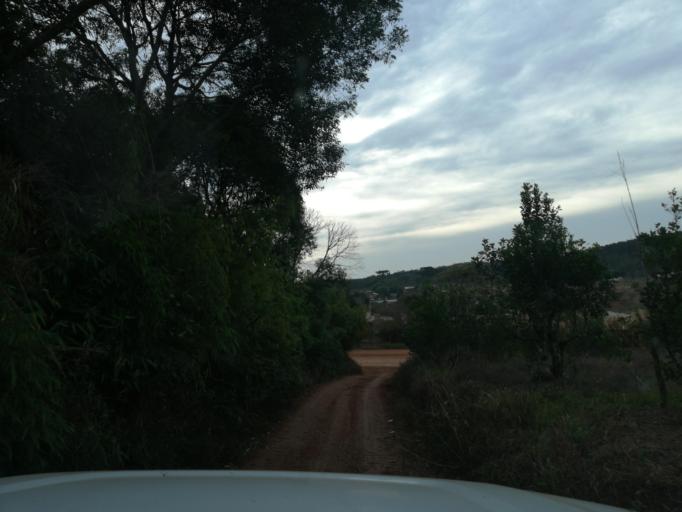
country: AR
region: Misiones
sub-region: Departamento de San Pedro
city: San Pedro
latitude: -26.6306
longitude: -54.0929
